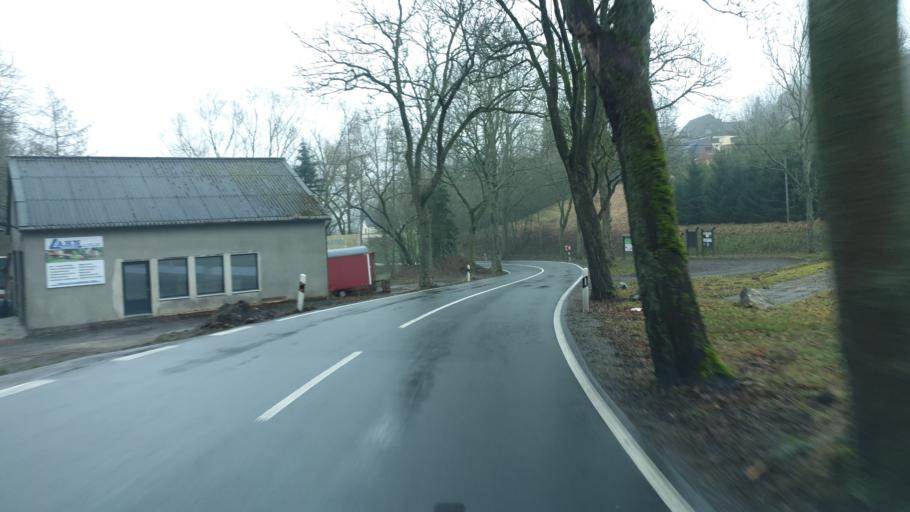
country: DE
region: Saxony
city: Neuhausen
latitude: 50.6817
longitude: 13.4612
